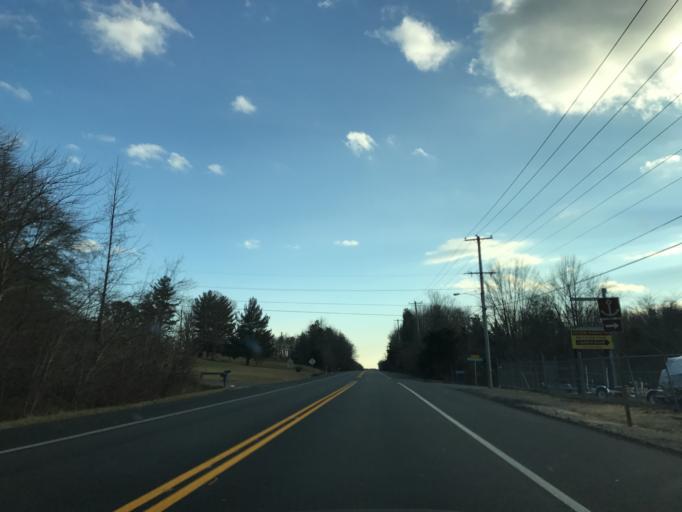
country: US
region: Maryland
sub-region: Cecil County
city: North East
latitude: 39.5908
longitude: -75.9419
